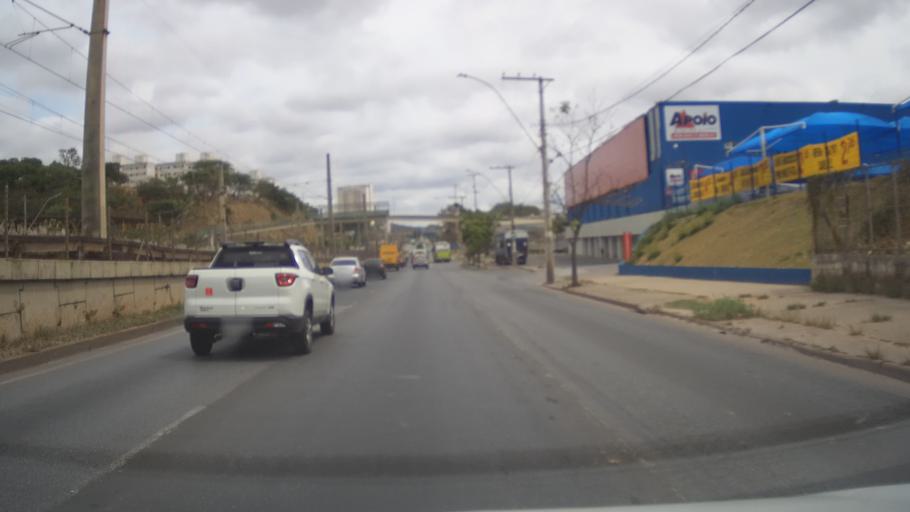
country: BR
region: Minas Gerais
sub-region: Belo Horizonte
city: Belo Horizonte
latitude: -19.8306
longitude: -43.9412
